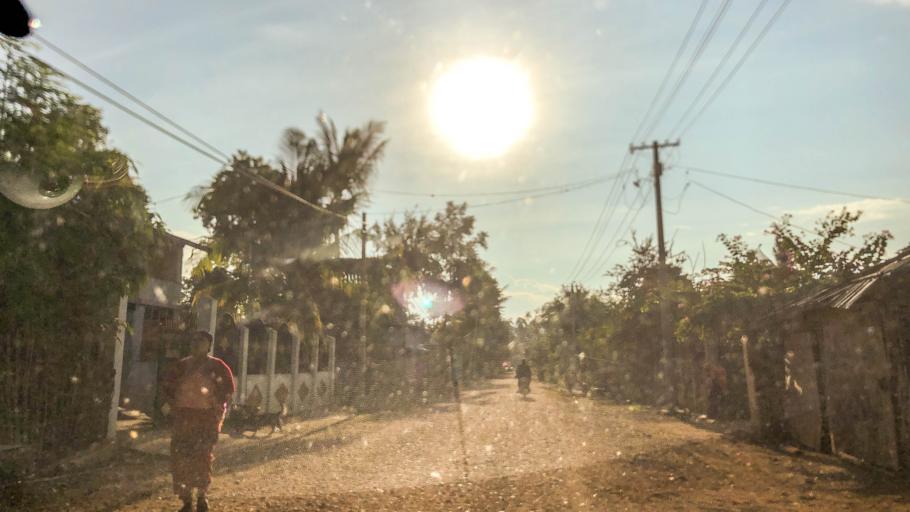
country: MM
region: Magway
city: Magway
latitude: 19.9743
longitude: 95.0375
